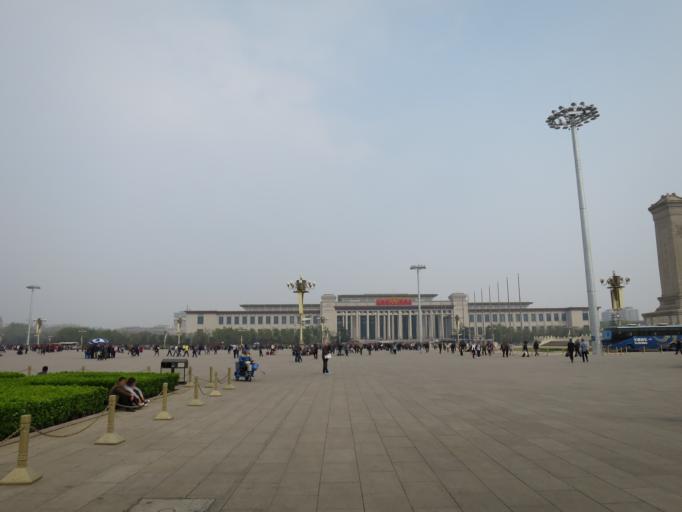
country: CN
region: Beijing
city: Beijing
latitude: 39.9040
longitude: 116.3900
